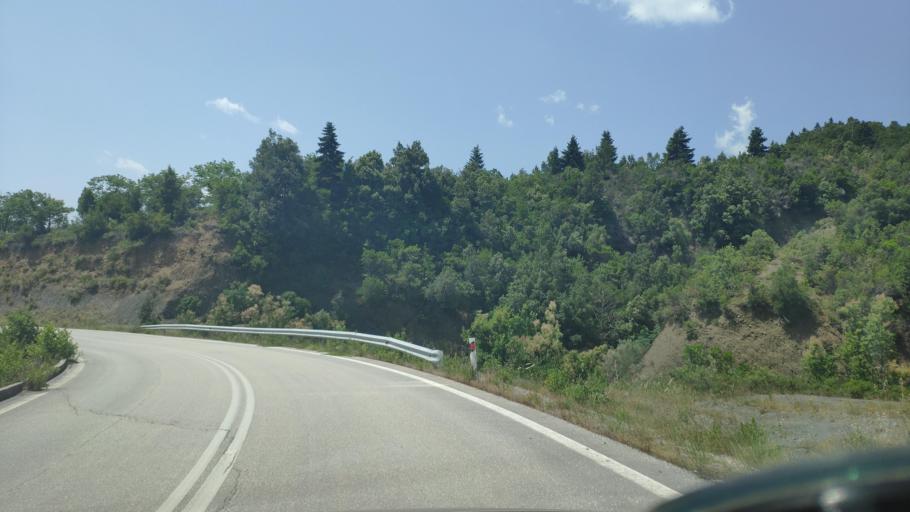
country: GR
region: Epirus
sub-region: Nomos Artas
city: Ano Kalentini
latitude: 39.2859
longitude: 21.3185
